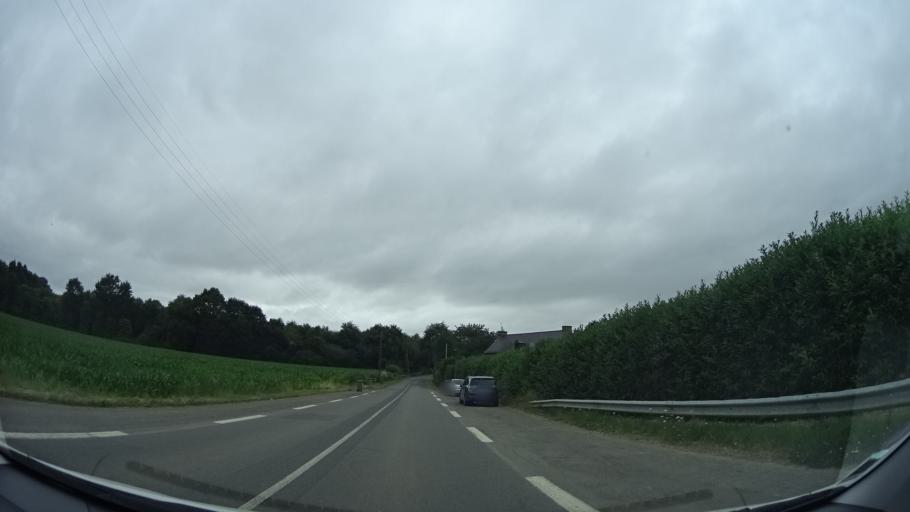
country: FR
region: Brittany
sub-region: Departement d'Ille-et-Vilaine
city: Quebriac
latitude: 48.3779
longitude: -1.8364
